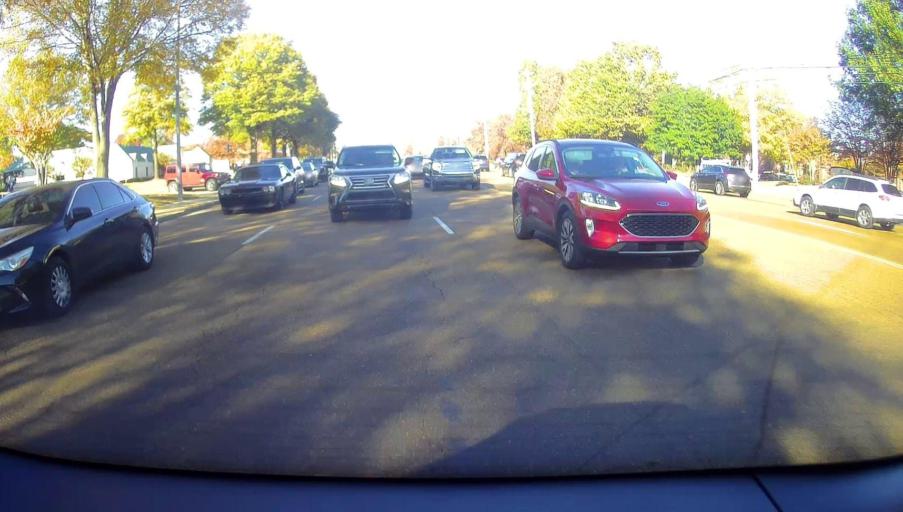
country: US
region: Tennessee
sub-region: Shelby County
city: Germantown
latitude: 35.1110
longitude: -89.8026
